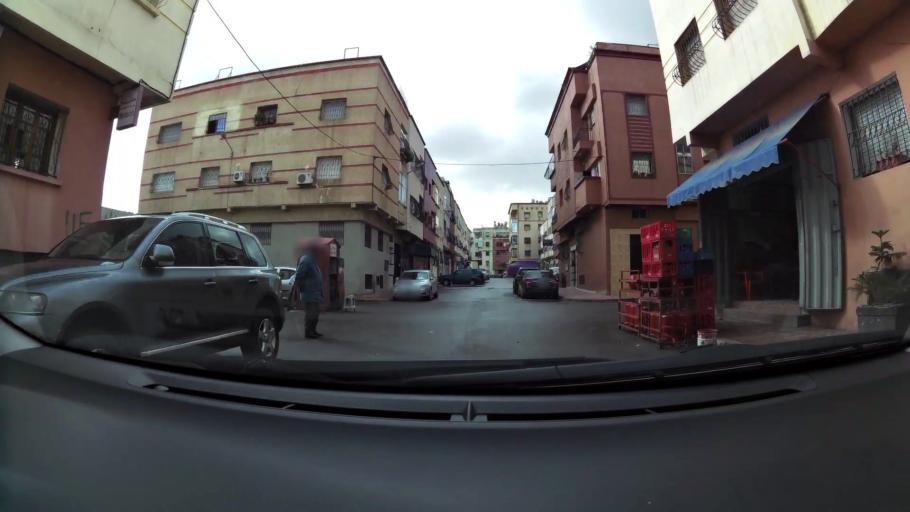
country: MA
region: Grand Casablanca
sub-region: Mediouna
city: Tit Mellil
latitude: 33.6016
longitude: -7.5355
